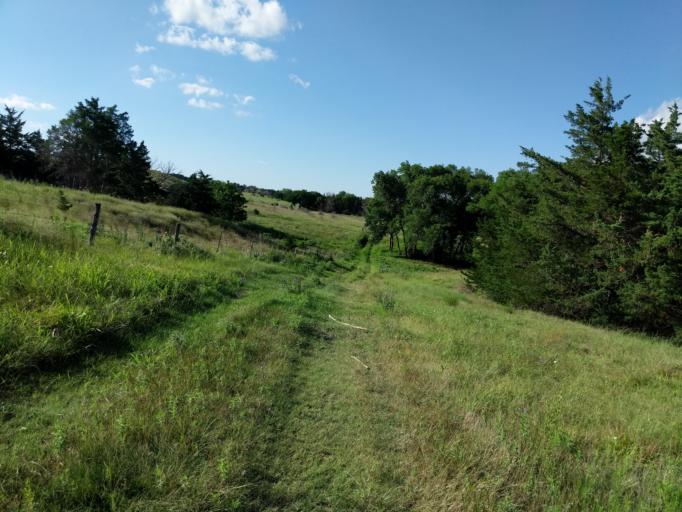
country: US
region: Kansas
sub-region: Smith County
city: Smith Center
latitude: 39.8906
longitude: -98.9498
